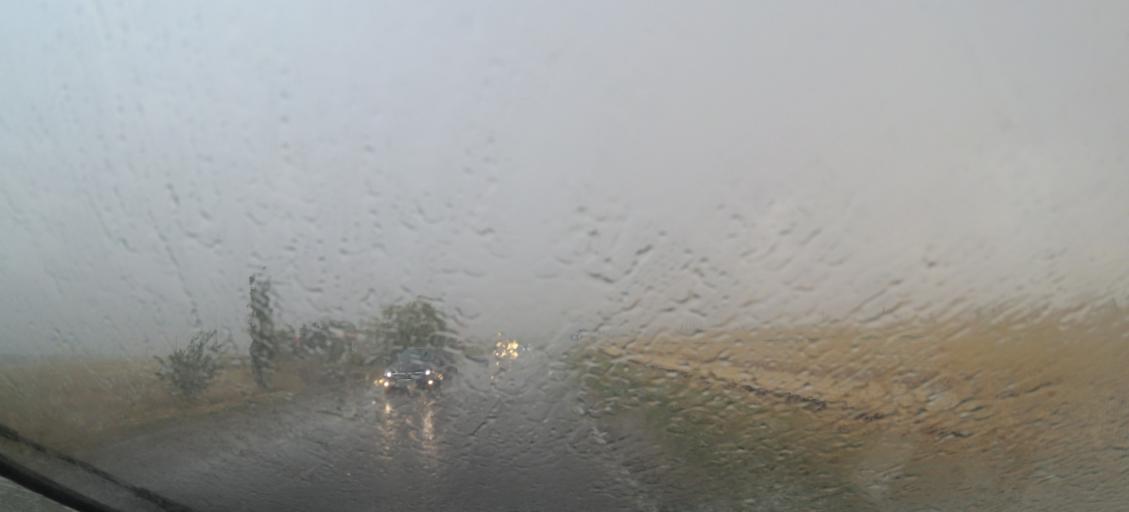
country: RU
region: Rostov
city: Proletarsk
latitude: 46.6755
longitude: 41.6999
